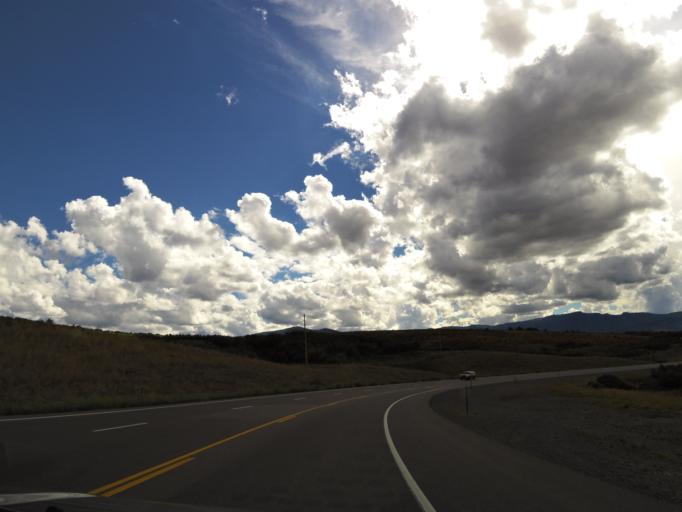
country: US
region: Colorado
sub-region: Hinsdale County
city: Lake City
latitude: 38.3936
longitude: -107.4546
